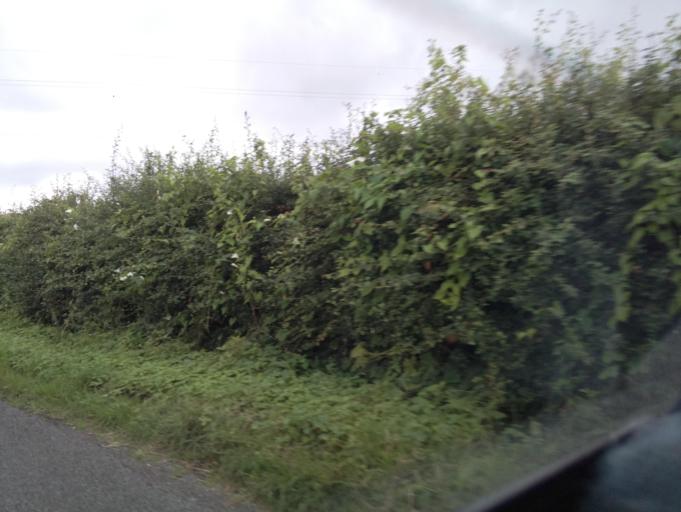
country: GB
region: England
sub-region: Solihull
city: Dickens Heath
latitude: 52.3791
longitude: -1.8407
